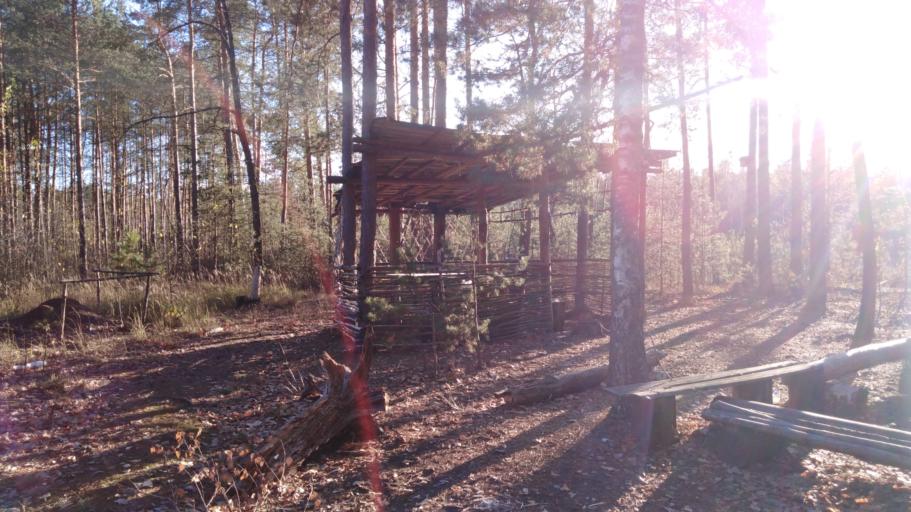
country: BY
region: Gomel
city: Gomel
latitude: 52.3831
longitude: 30.7761
